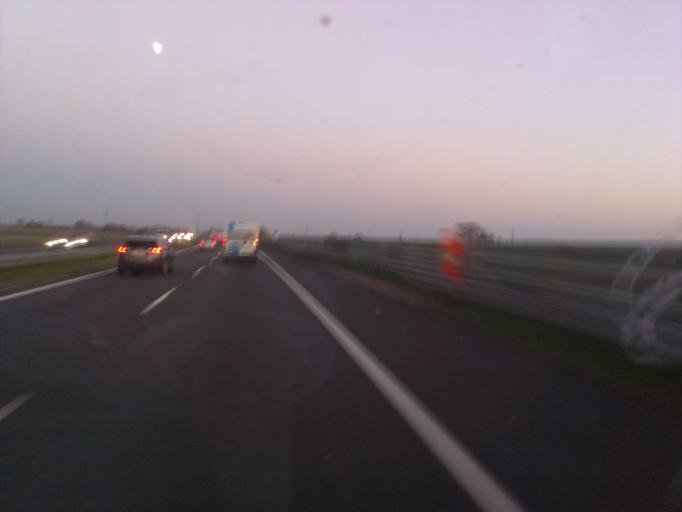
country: PL
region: Silesian Voivodeship
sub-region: Powiat gliwicki
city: Sosnicowice
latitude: 50.3499
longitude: 18.5309
